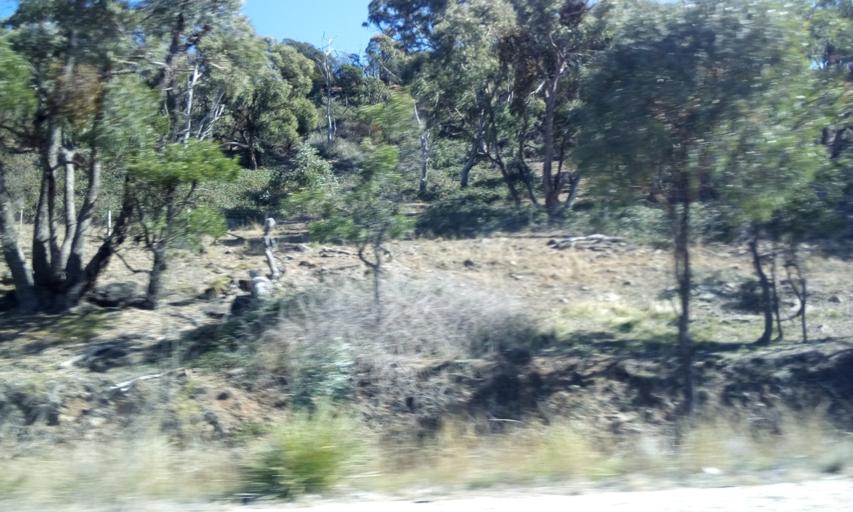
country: AU
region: New South Wales
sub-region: Yass Valley
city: Gundaroo
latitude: -35.0959
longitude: 149.3762
